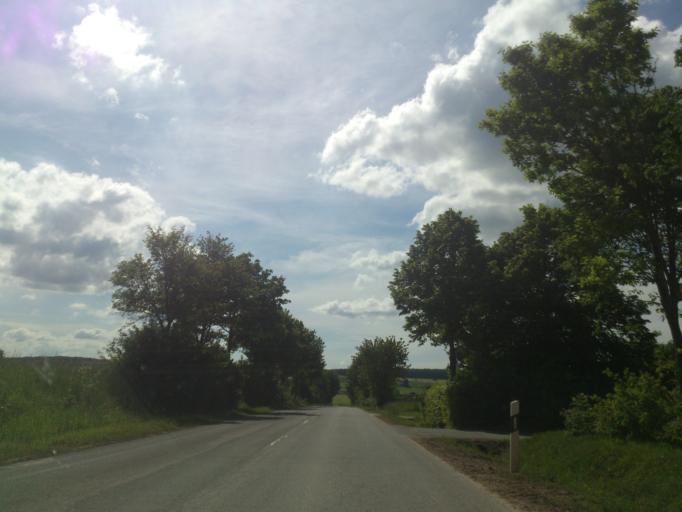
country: DE
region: North Rhine-Westphalia
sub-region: Regierungsbezirk Detmold
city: Willebadessen
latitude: 51.6559
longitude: 9.0757
